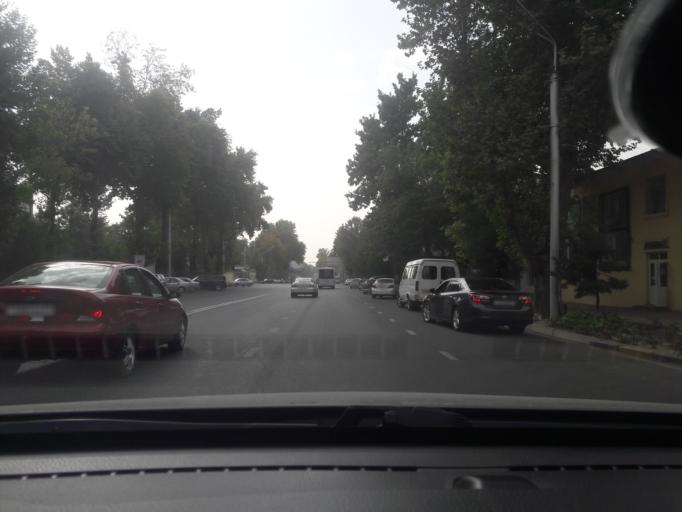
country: TJ
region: Dushanbe
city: Dushanbe
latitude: 38.5770
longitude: 68.8031
